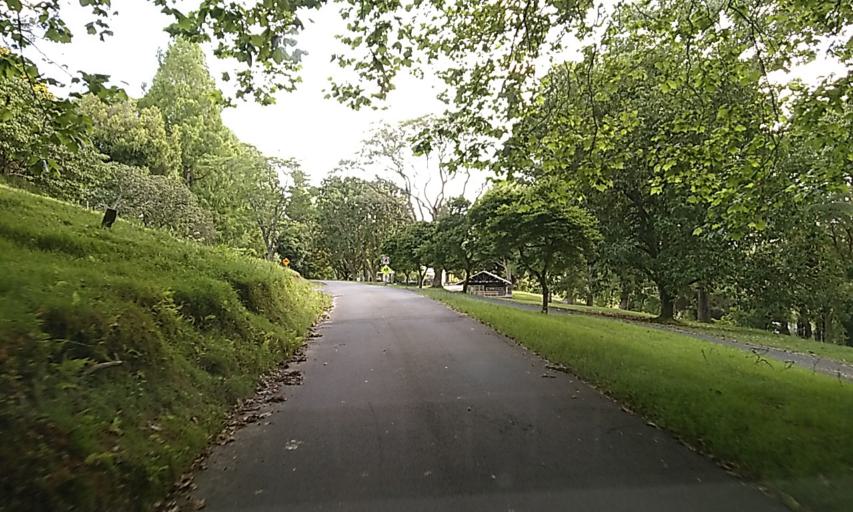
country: NZ
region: Bay of Plenty
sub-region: Tauranga City
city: Tauranga
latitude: -37.8085
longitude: 176.0459
